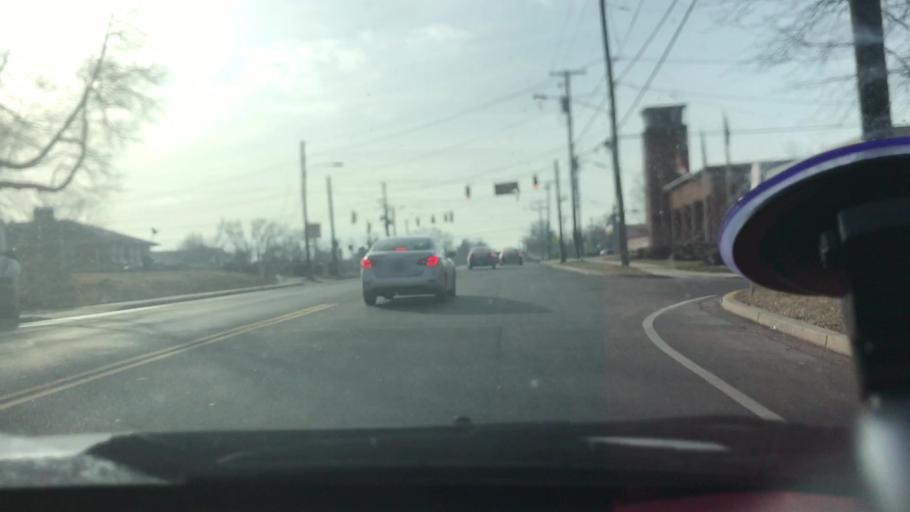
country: US
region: Maryland
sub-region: Prince George's County
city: Seat Pleasant
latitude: 38.8885
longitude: -76.8986
